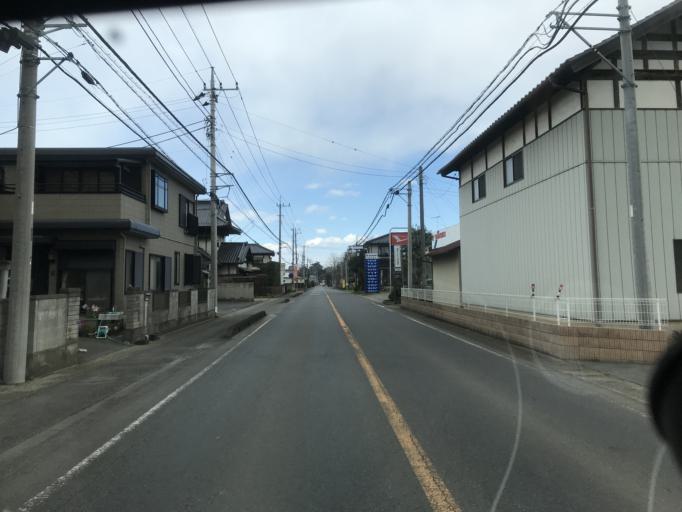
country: JP
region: Ibaraki
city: Shimodate
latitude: 36.2413
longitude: 139.9772
